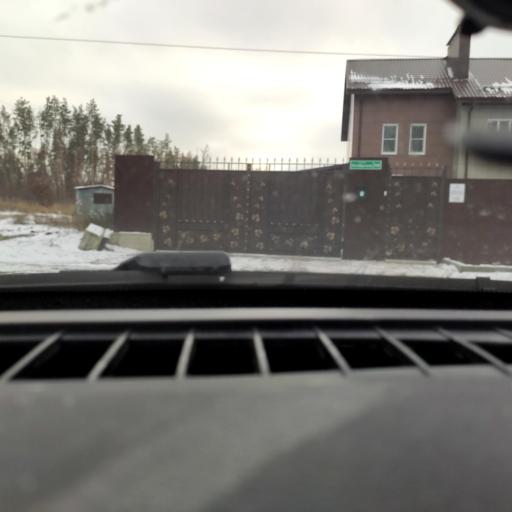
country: RU
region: Voronezj
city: Podgornoye
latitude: 51.8033
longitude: 39.1451
